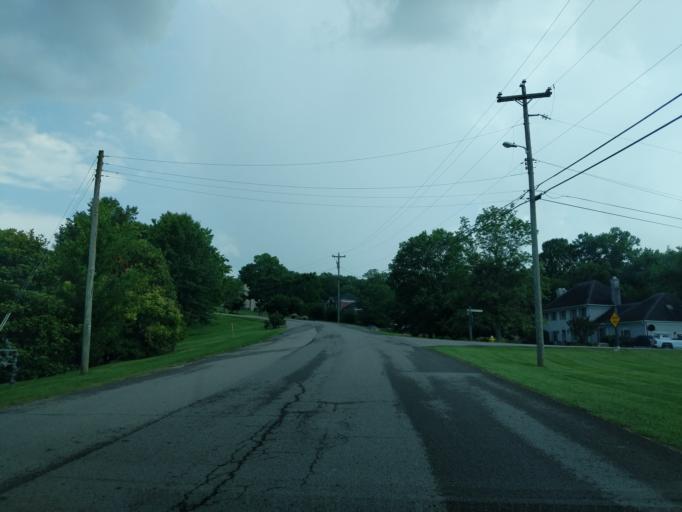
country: US
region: Tennessee
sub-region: Cheatham County
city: Pegram
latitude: 36.0285
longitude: -86.9593
